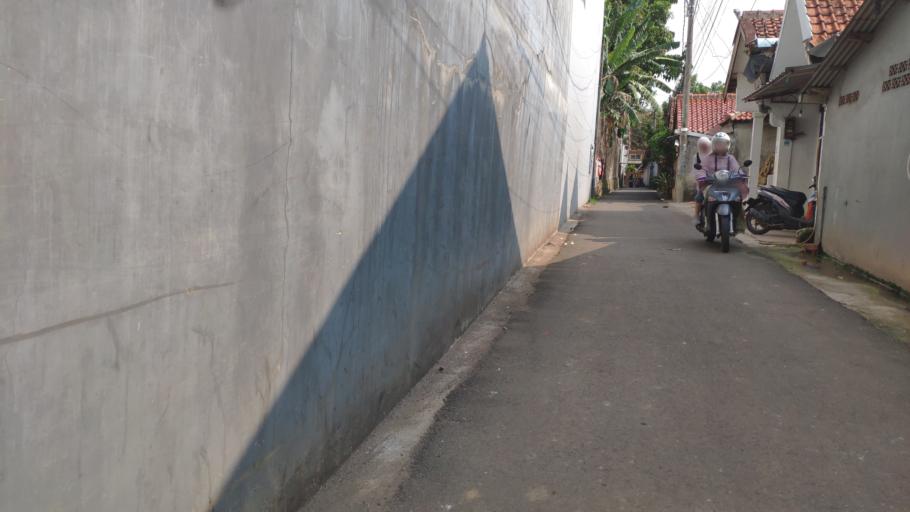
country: ID
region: West Java
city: Depok
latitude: -6.3232
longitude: 106.8134
